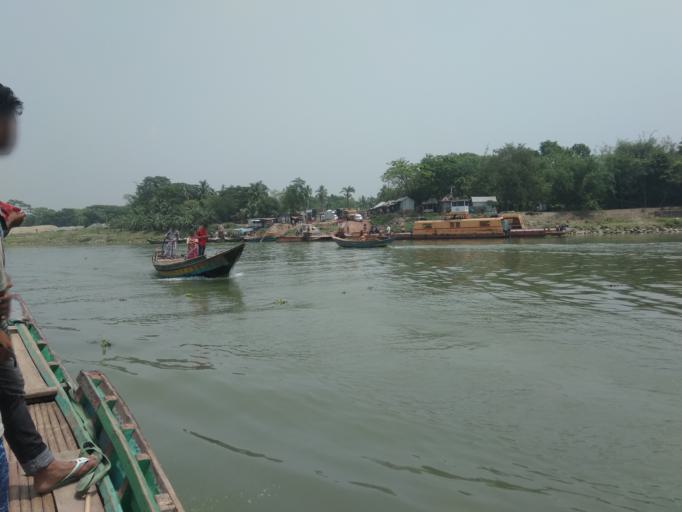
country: BD
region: Khulna
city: Kalia
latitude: 23.1948
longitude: 89.6925
